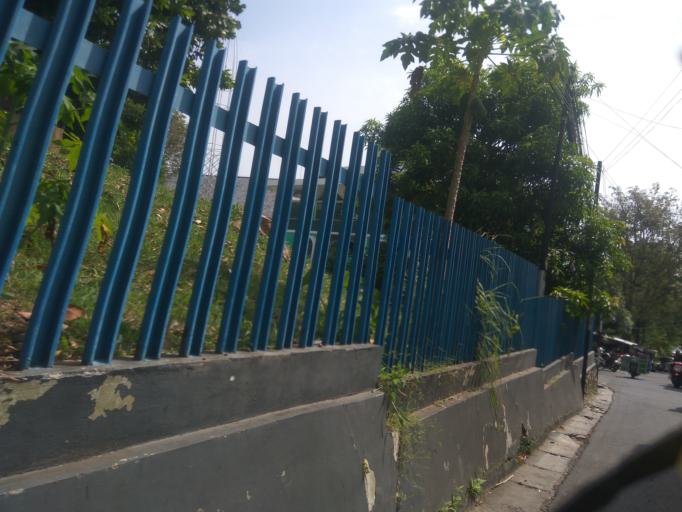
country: ID
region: Central Java
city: Semarang
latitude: -7.0534
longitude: 110.4357
